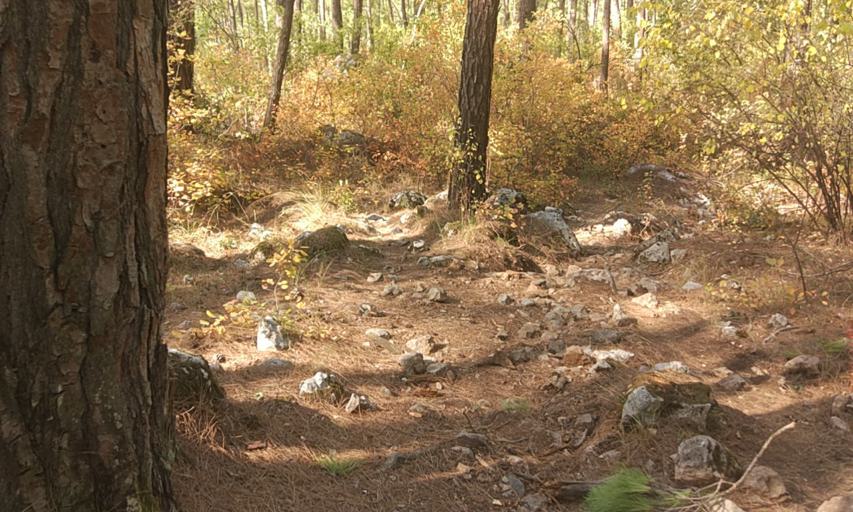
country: TR
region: Antalya
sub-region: Kemer
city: Goeynuek
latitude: 36.6751
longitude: 30.4975
